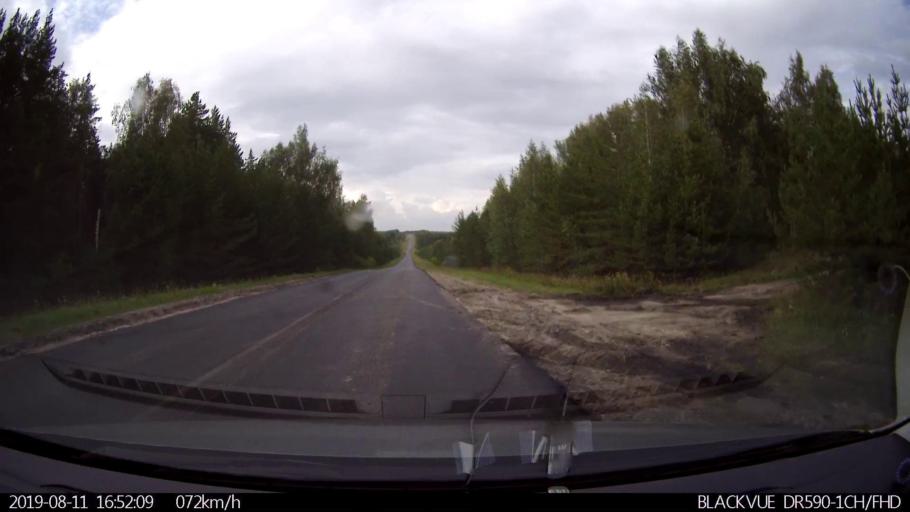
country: RU
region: Ulyanovsk
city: Mayna
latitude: 54.2446
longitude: 47.6750
